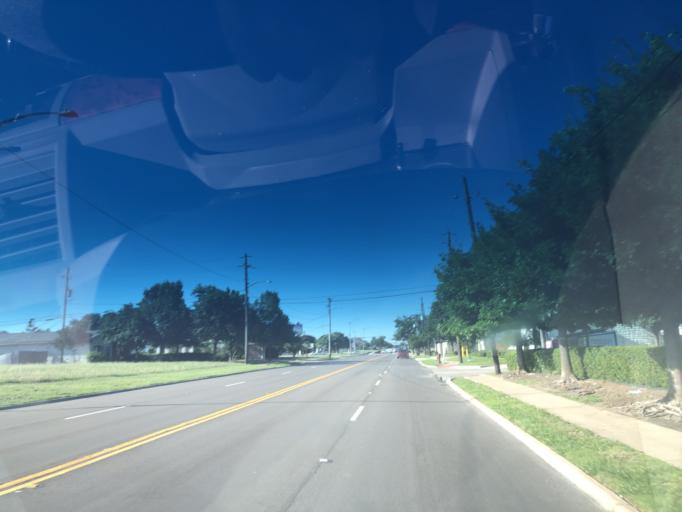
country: US
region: Texas
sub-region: Dallas County
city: Grand Prairie
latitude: 32.7117
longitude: -97.0198
